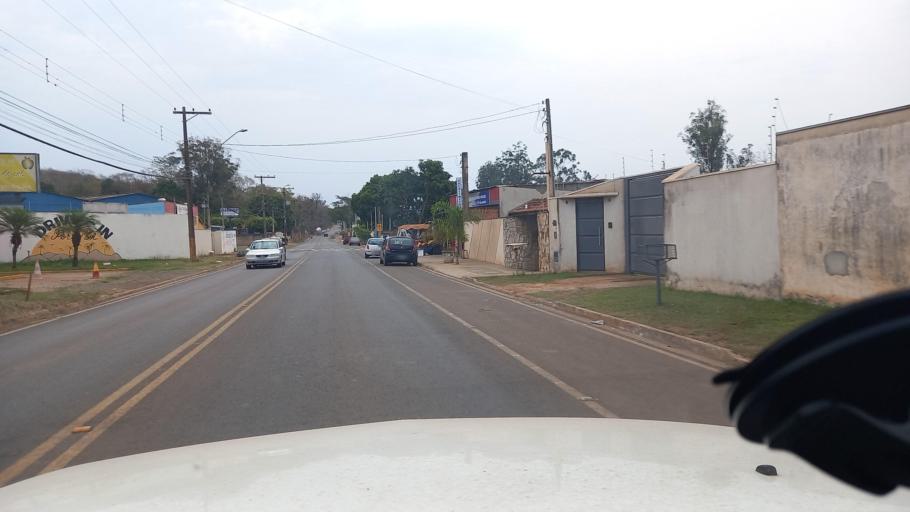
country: BR
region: Sao Paulo
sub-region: Moji-Guacu
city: Mogi-Gaucu
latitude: -22.3788
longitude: -46.9594
